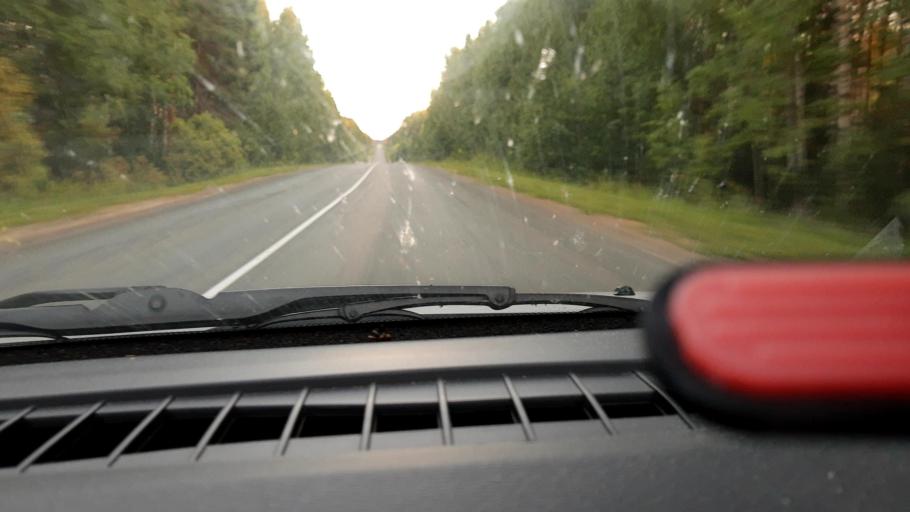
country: RU
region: Nizjnij Novgorod
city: Tonkino
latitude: 57.2983
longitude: 46.4625
